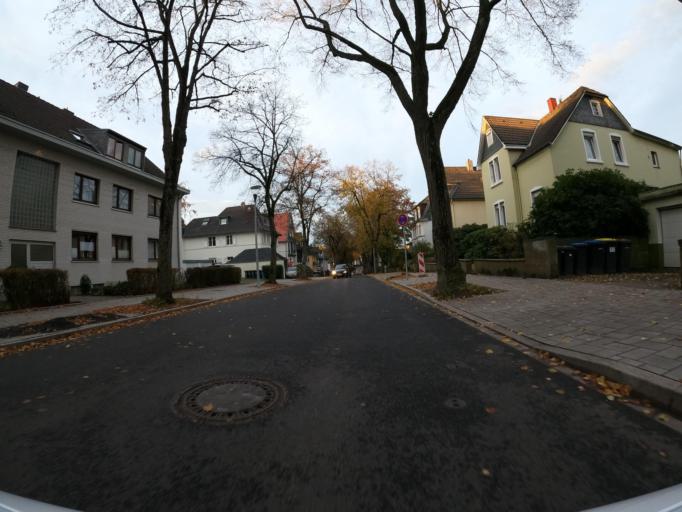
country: DE
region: North Rhine-Westphalia
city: Haan
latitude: 51.1919
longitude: 7.0070
